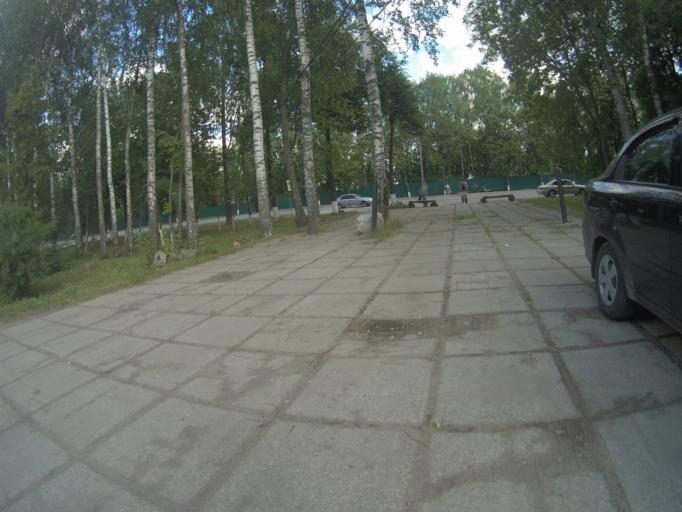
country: RU
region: Vladimir
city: Bogolyubovo
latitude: 56.1728
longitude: 40.4923
